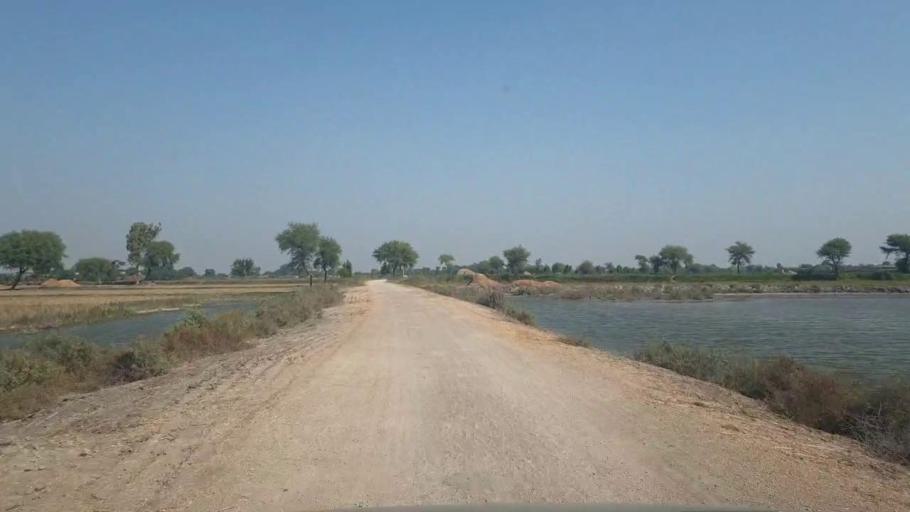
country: PK
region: Sindh
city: Badin
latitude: 24.6795
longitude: 68.8613
